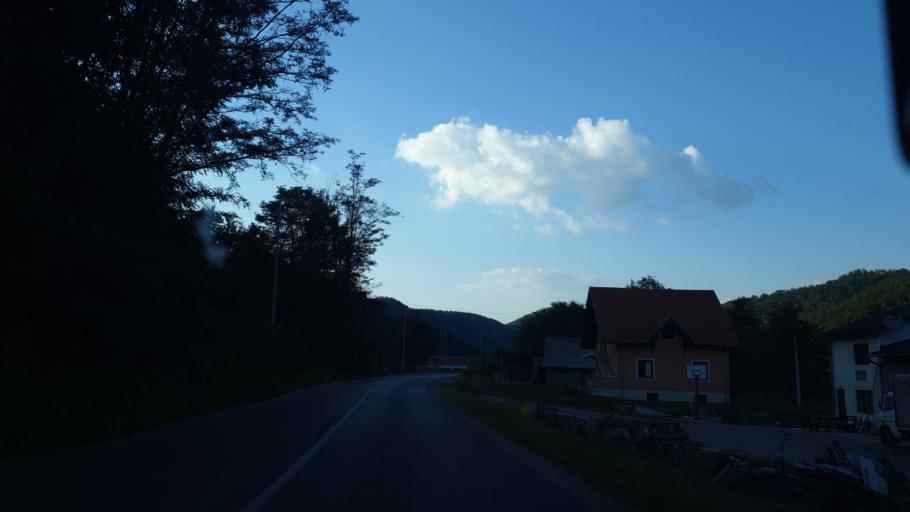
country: RS
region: Central Serbia
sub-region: Zlatiborski Okrug
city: Pozega
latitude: 43.9176
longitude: 20.0051
